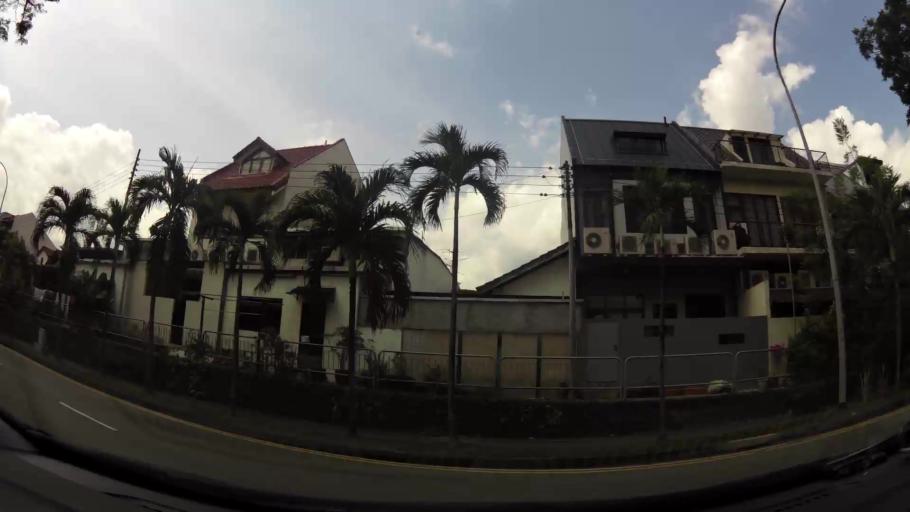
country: SG
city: Singapore
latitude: 1.3758
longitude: 103.8284
